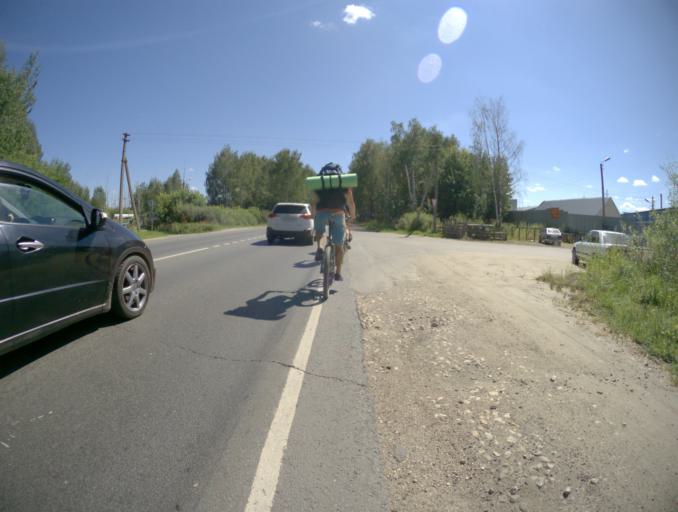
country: RU
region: Nizjnij Novgorod
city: Neklyudovo
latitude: 56.4190
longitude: 43.9993
